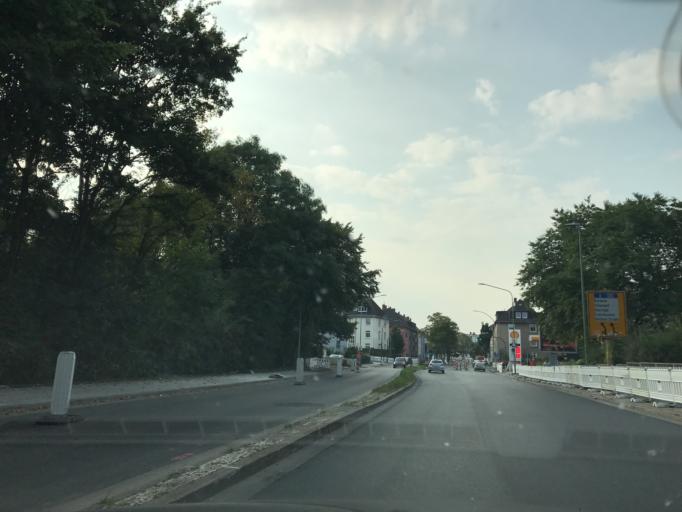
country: DE
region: North Rhine-Westphalia
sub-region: Regierungsbezirk Dusseldorf
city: Essen
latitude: 51.4416
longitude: 6.9772
